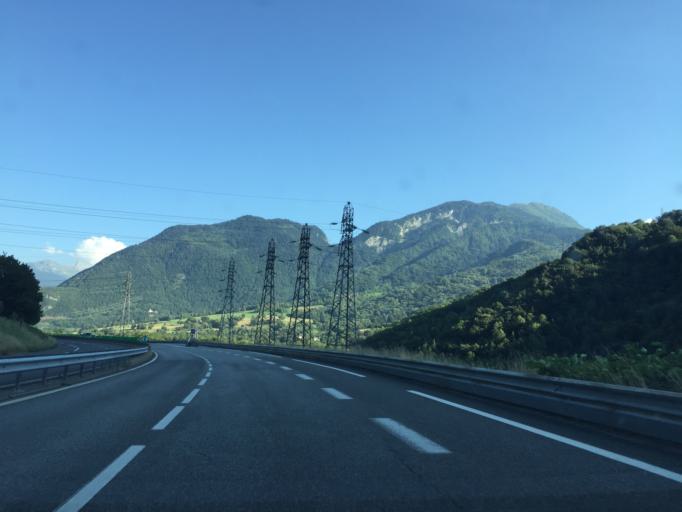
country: FR
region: Rhone-Alpes
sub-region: Departement de la Savoie
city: Aigueblanche
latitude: 45.5166
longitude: 6.4867
